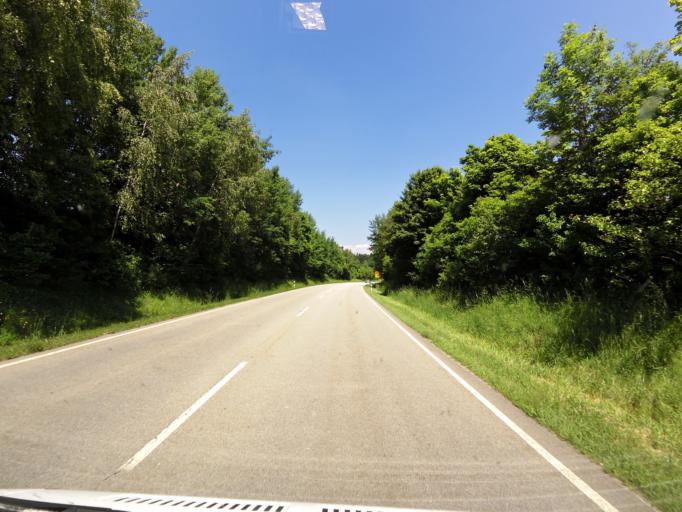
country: DE
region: Bavaria
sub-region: Lower Bavaria
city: Buchlberg
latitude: 48.6967
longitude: 13.5093
